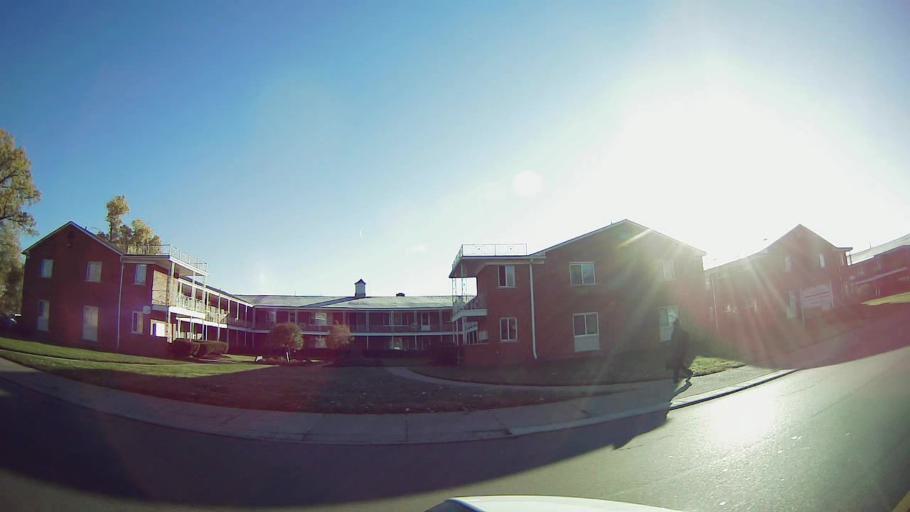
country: US
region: Michigan
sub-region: Oakland County
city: Oak Park
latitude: 42.4182
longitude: -83.1702
